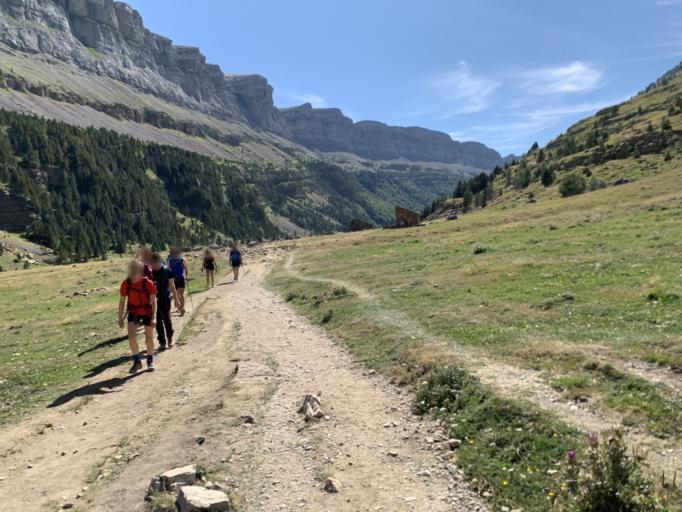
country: ES
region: Aragon
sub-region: Provincia de Huesca
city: Broto
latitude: 42.6431
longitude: 0.0079
